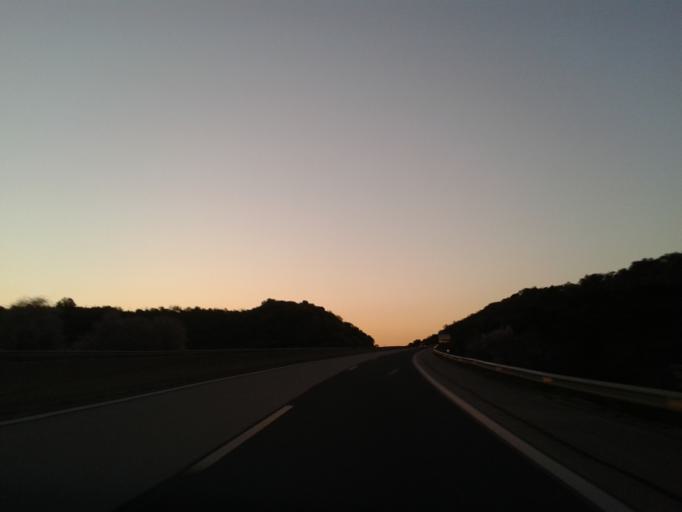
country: PT
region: Faro
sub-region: Loule
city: Boliqueime
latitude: 37.1576
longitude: -8.1804
